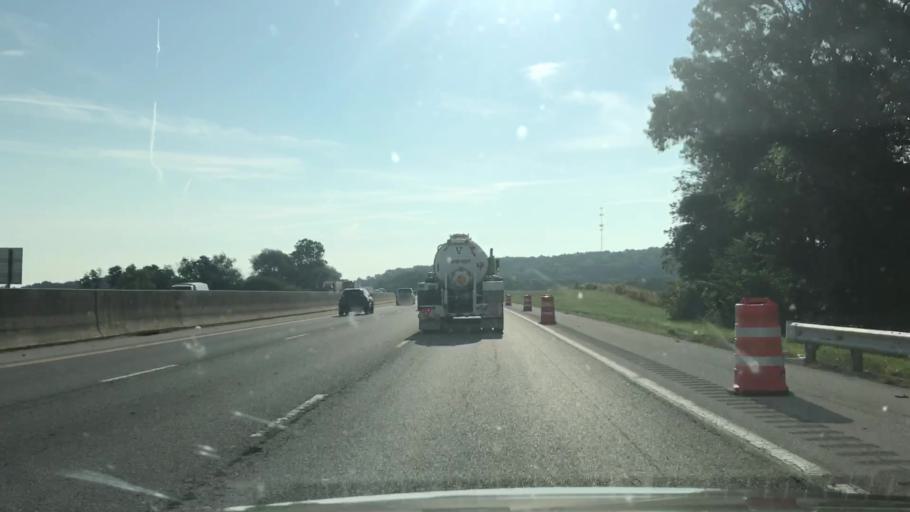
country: US
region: Kentucky
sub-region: Edmonson County
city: Brownsville
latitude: 37.0413
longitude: -86.1895
